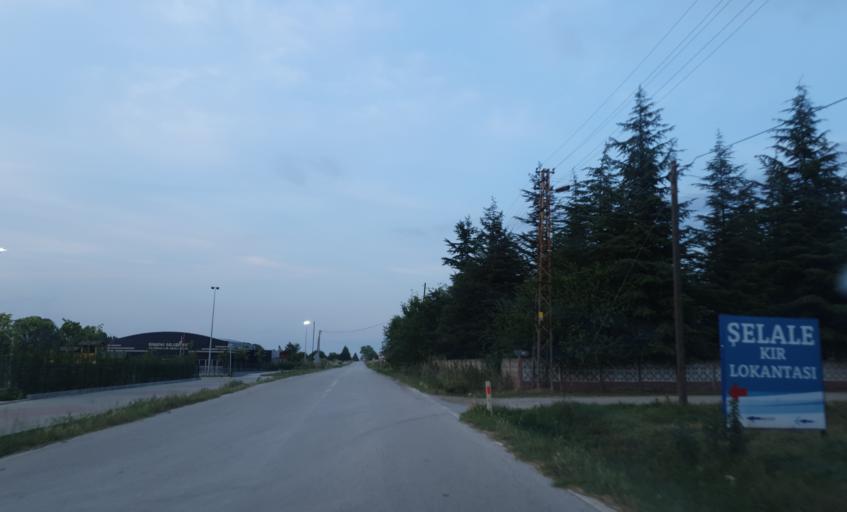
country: TR
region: Tekirdag
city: Beyazkoy
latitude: 41.3883
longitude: 27.6237
